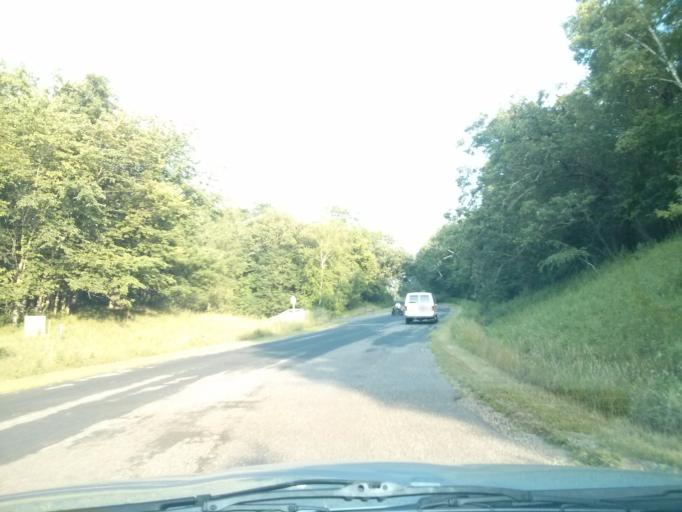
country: US
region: Wisconsin
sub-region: Saint Croix County
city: North Hudson
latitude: 45.0129
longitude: -92.6934
